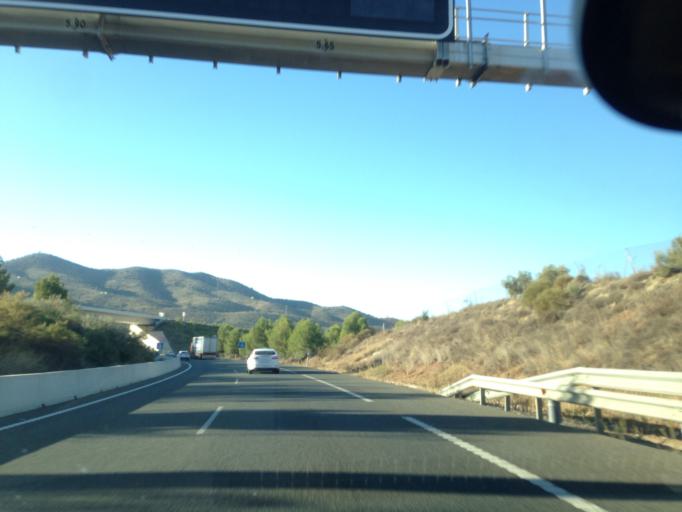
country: ES
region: Andalusia
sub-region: Provincia de Malaga
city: Casabermeja
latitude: 36.9099
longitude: -4.4458
